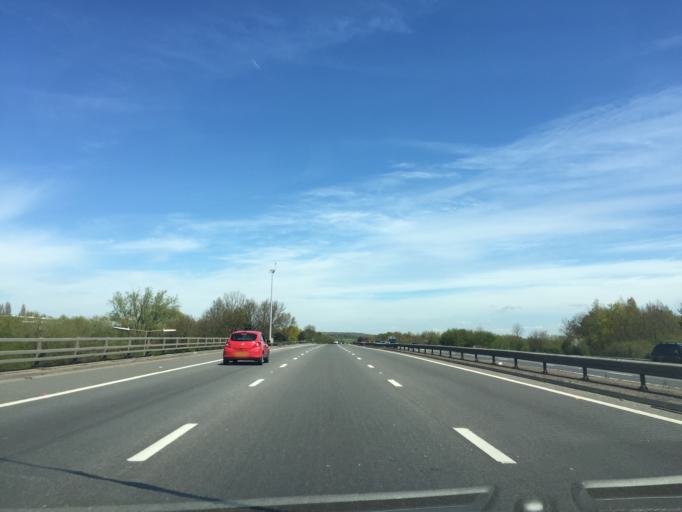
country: GB
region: England
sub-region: Essex
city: Chigwell
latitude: 51.6403
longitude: 0.0837
